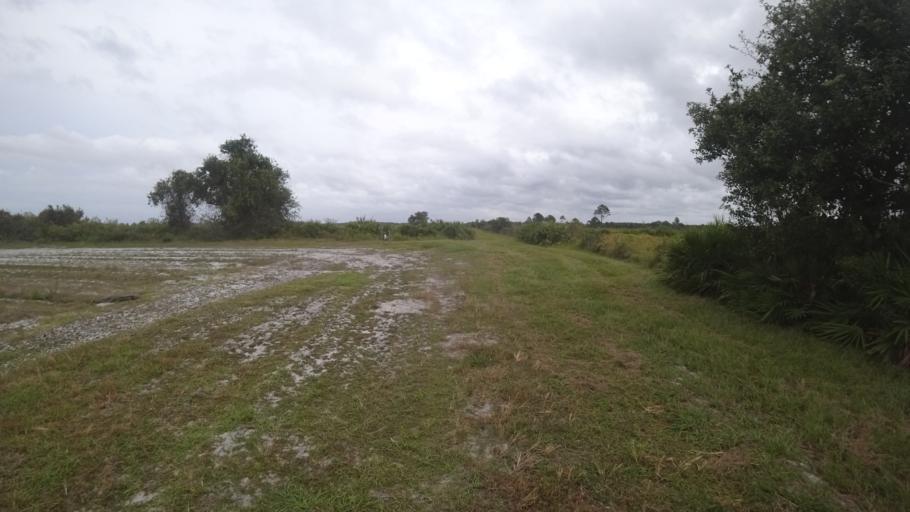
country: US
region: Florida
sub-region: Hillsborough County
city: Wimauma
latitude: 27.5599
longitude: -82.1296
